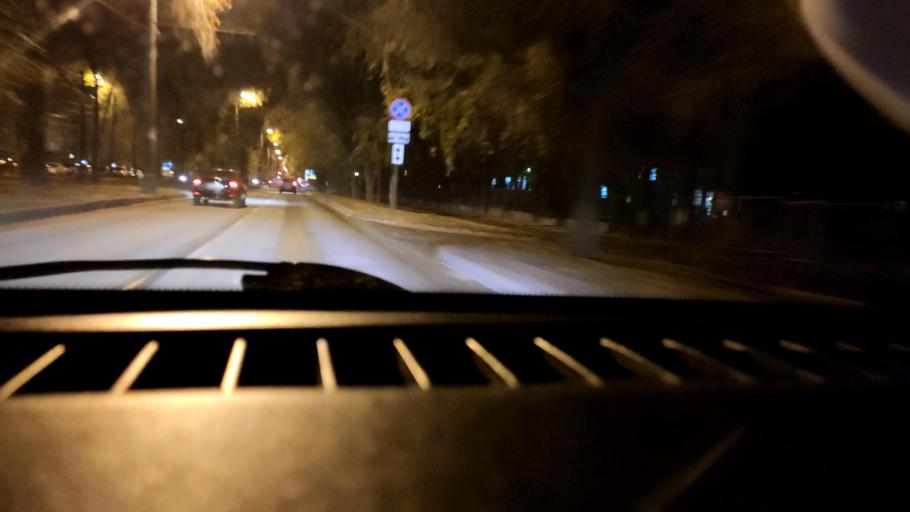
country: RU
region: Samara
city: Samara
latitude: 53.2202
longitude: 50.2451
